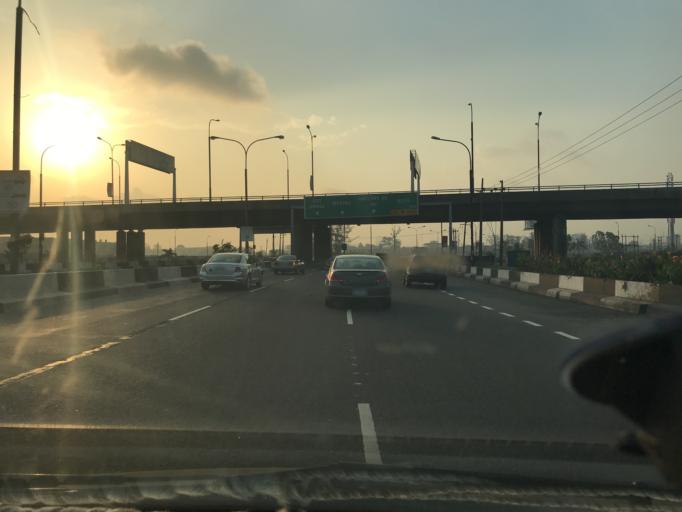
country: NG
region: Lagos
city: Lagos
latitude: 6.4568
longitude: 3.4074
